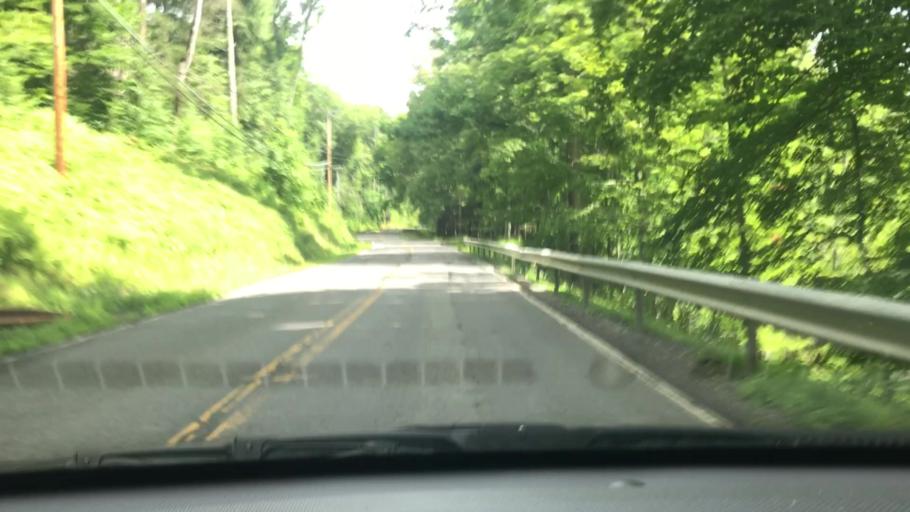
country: US
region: New York
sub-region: Ulster County
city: Shokan
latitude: 41.9804
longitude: -74.2763
